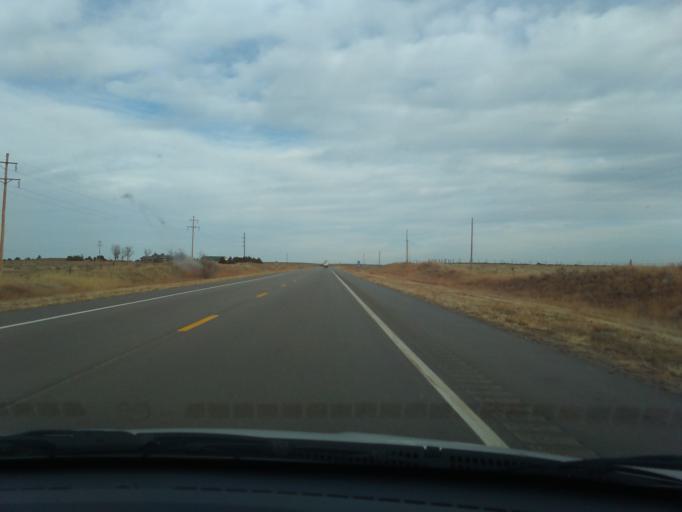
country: US
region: Nebraska
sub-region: Dundy County
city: Benkelman
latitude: 40.0664
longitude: -101.5243
